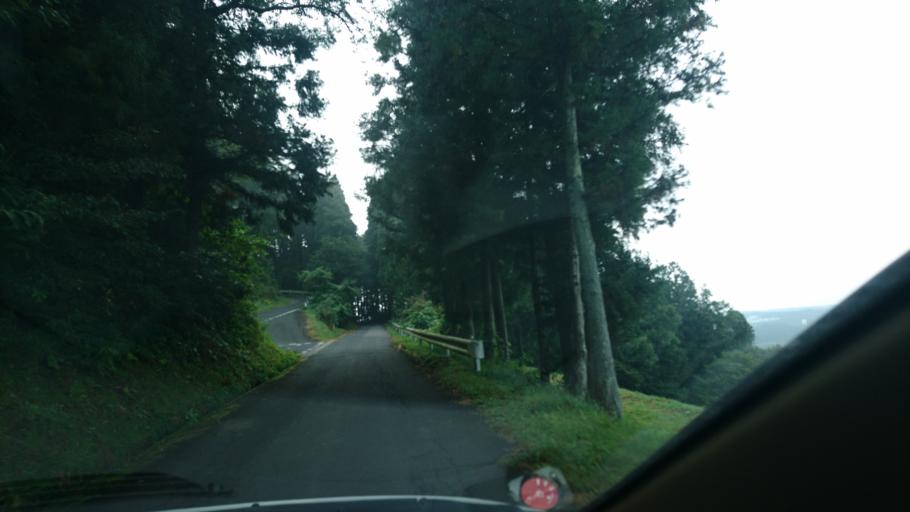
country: JP
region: Iwate
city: Ichinoseki
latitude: 38.9606
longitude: 141.1832
